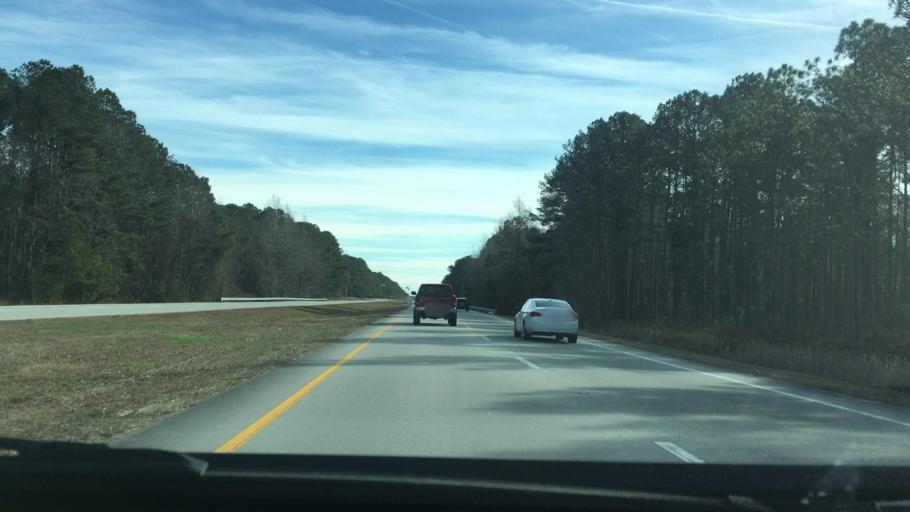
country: US
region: North Carolina
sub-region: Carteret County
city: Newport
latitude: 34.7734
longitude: -76.8687
